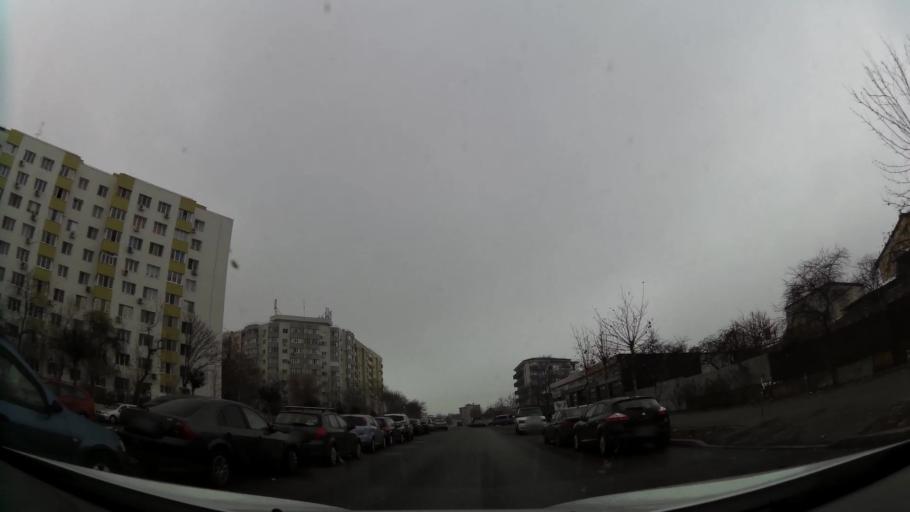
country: RO
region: Ilfov
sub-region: Comuna Popesti-Leordeni
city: Popesti-Leordeni
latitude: 44.4105
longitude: 26.1634
